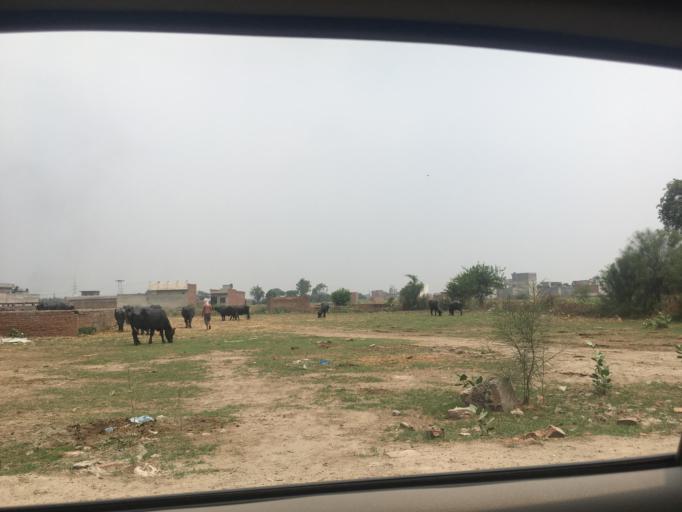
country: PK
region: Punjab
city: Lahore
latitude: 31.6230
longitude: 74.3471
